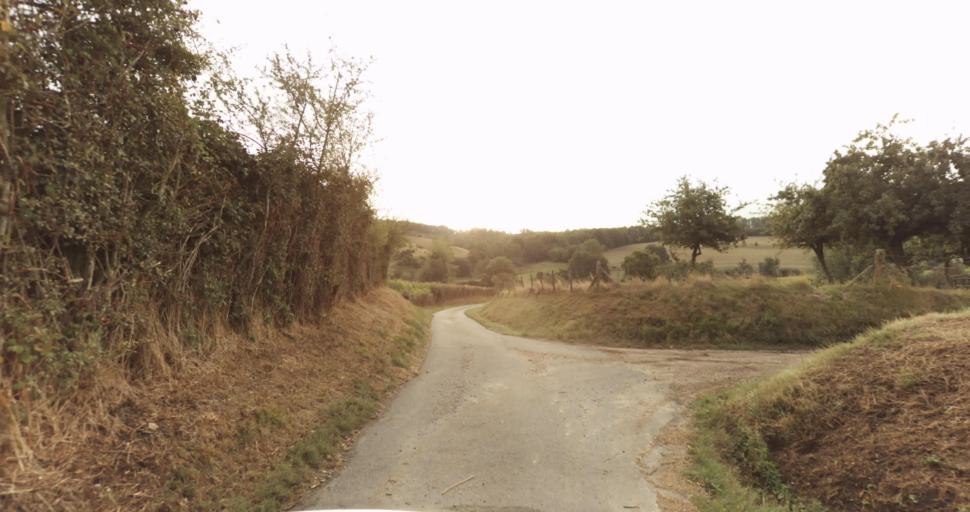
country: FR
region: Lower Normandy
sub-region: Departement de l'Orne
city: Trun
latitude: 48.8979
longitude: 0.0975
